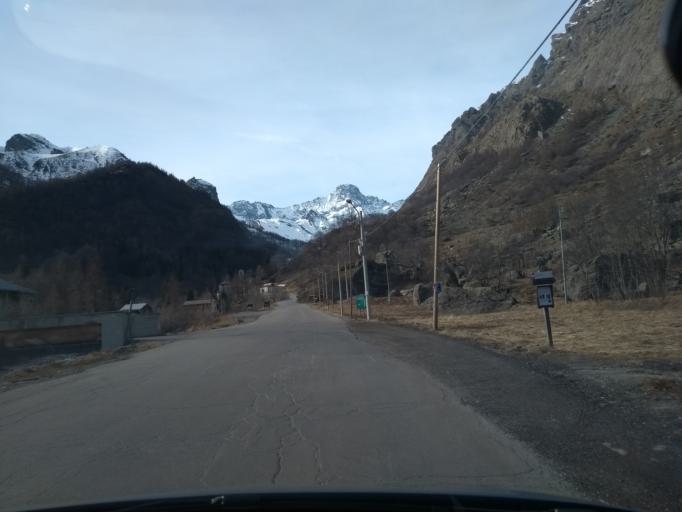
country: IT
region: Piedmont
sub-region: Provincia di Torino
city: Balme
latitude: 45.3032
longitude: 7.2247
